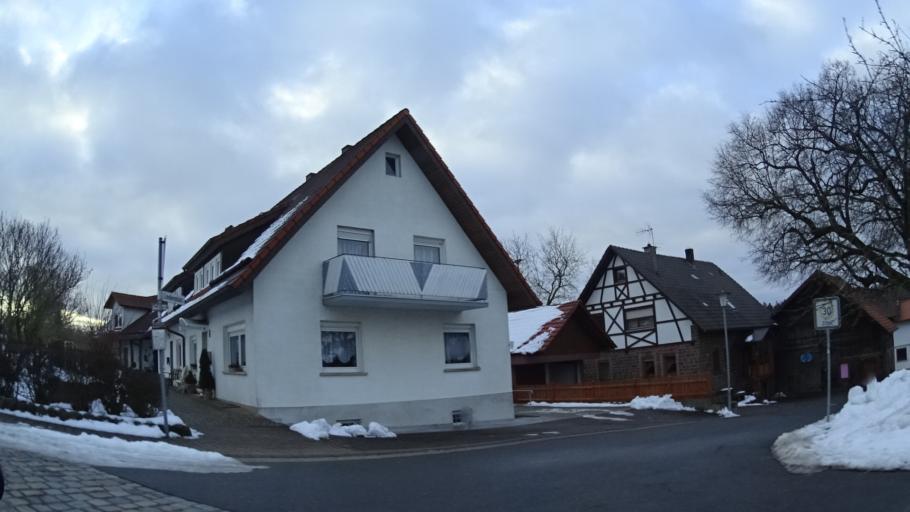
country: DE
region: Baden-Wuerttemberg
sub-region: Karlsruhe Region
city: Fahrenbach
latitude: 49.4730
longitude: 9.1543
